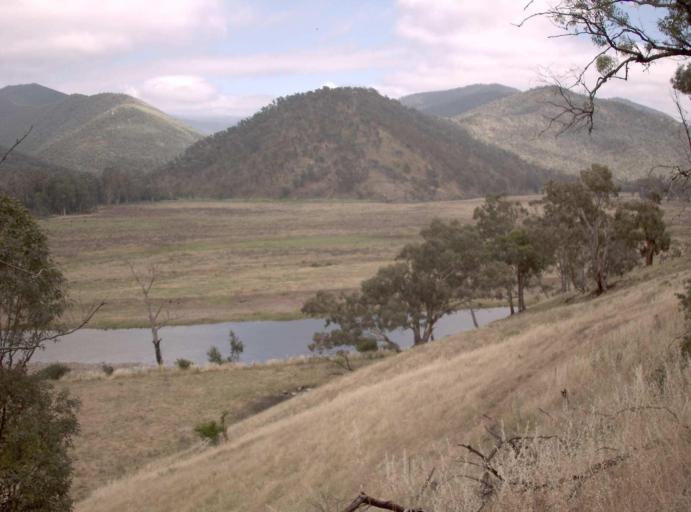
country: AU
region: Victoria
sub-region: Wellington
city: Heyfield
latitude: -37.6674
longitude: 146.6465
